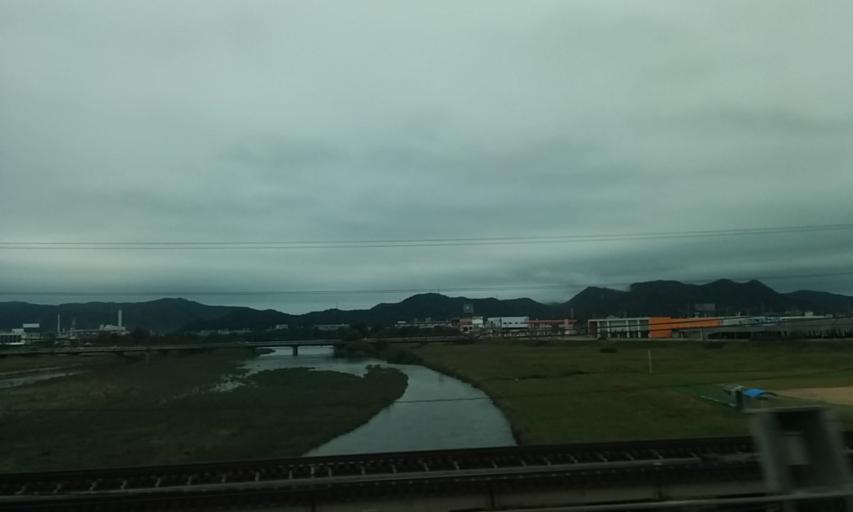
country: JP
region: Hyogo
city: Himeji
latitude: 34.8233
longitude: 134.7174
